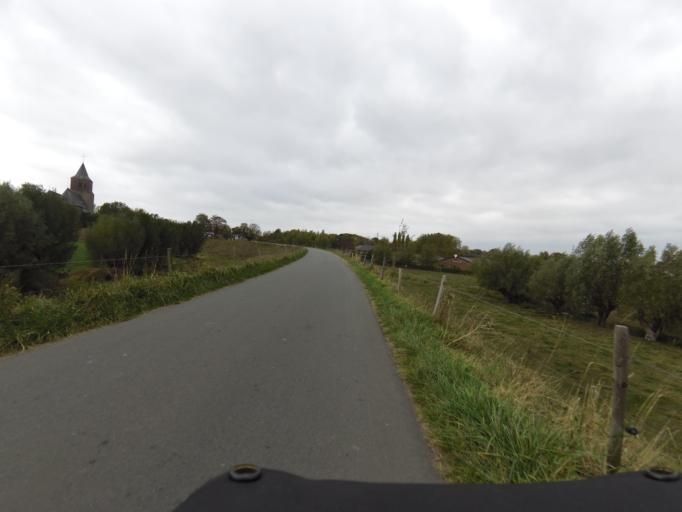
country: NL
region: Gelderland
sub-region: Gemeente Zevenaar
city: Zevenaar
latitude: 51.9134
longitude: 6.0864
